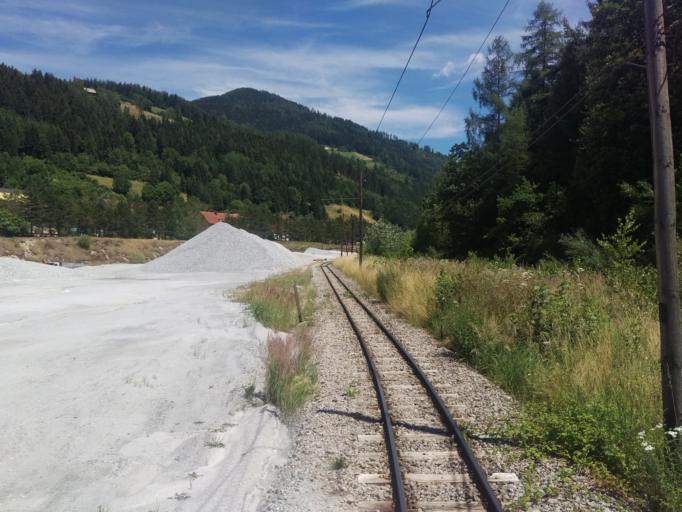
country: AT
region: Styria
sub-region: Politischer Bezirk Bruck-Muerzzuschlag
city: Allerheiligen im Muerztal
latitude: 47.3894
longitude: 15.4323
